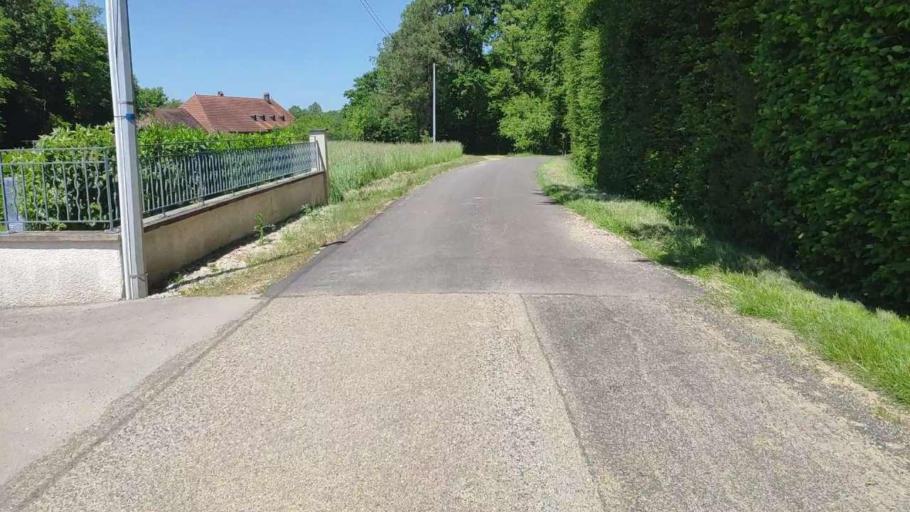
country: FR
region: Franche-Comte
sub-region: Departement du Jura
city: Bletterans
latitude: 46.7464
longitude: 5.4120
